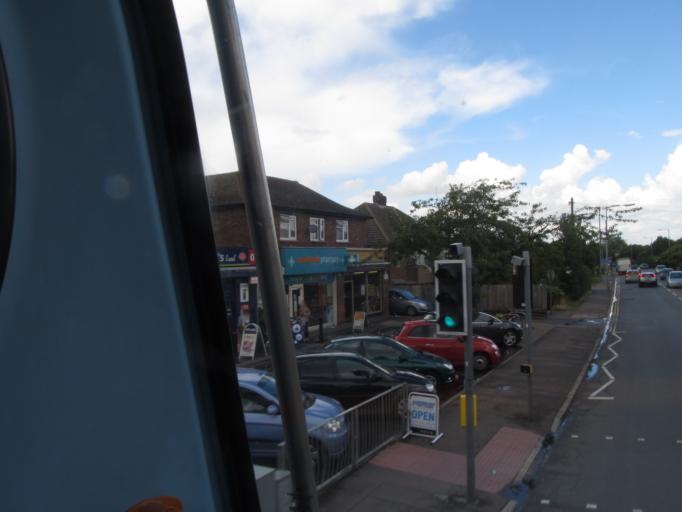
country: GB
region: England
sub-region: Cambridgeshire
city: Cambridge
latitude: 52.2201
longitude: 0.1117
